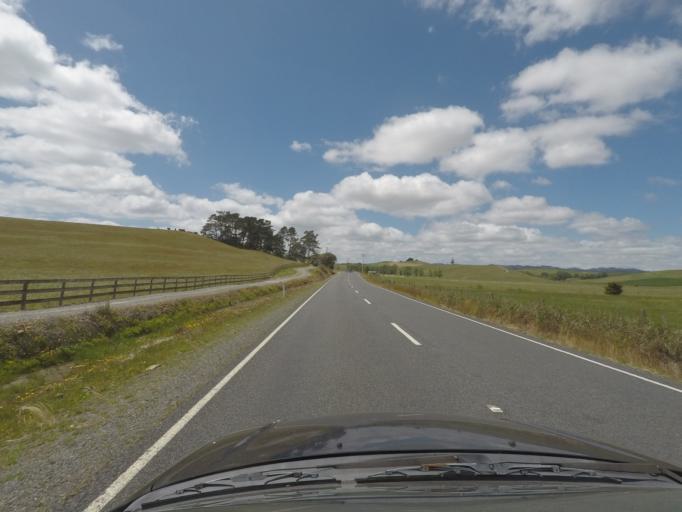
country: NZ
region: Northland
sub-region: Whangarei
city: Ruakaka
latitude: -35.9918
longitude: 174.4608
